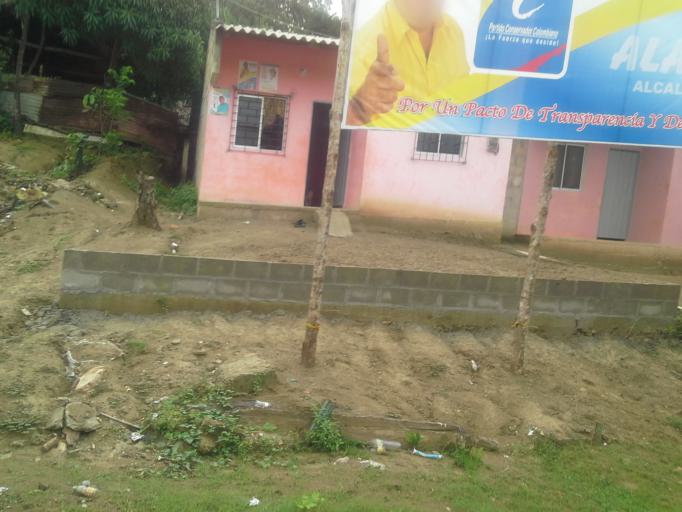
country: CO
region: Sucre
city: Coloso
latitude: 9.4622
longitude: -75.3683
